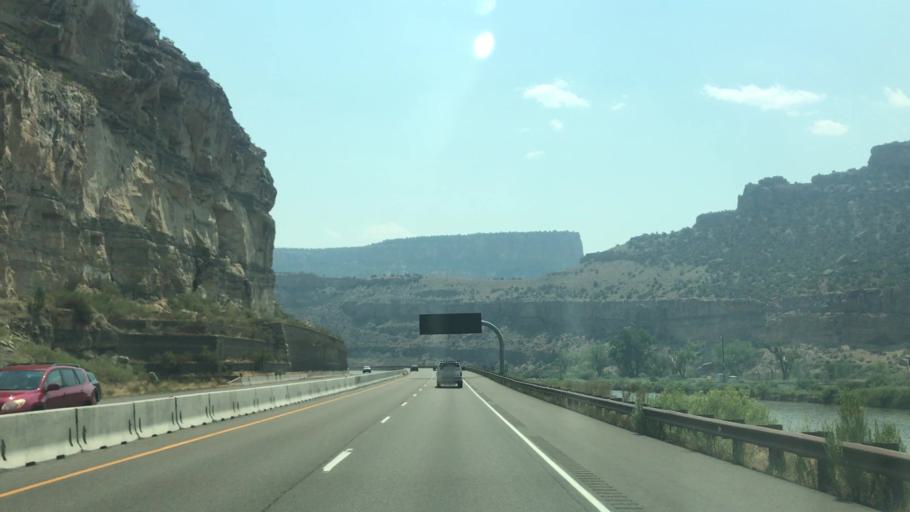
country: US
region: Colorado
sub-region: Mesa County
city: Palisade
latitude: 39.2029
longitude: -108.2660
